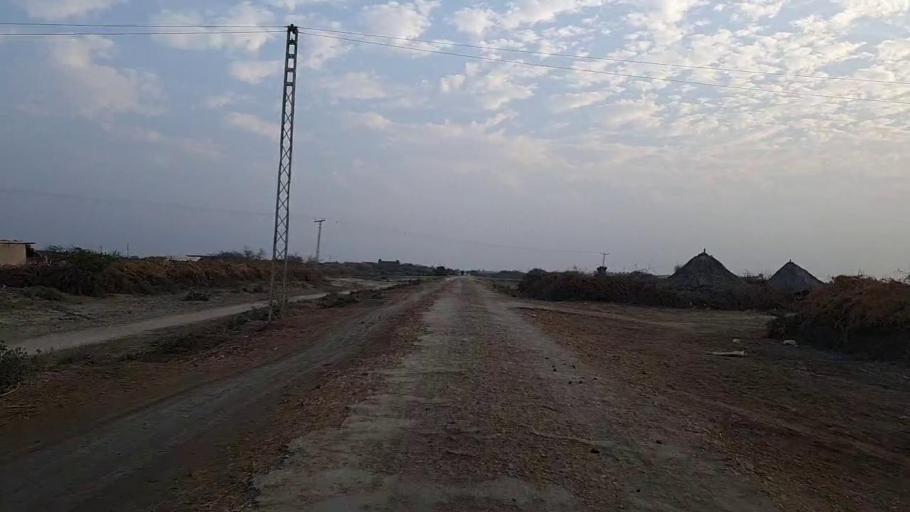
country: PK
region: Sindh
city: Pithoro
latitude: 25.4561
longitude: 69.3454
